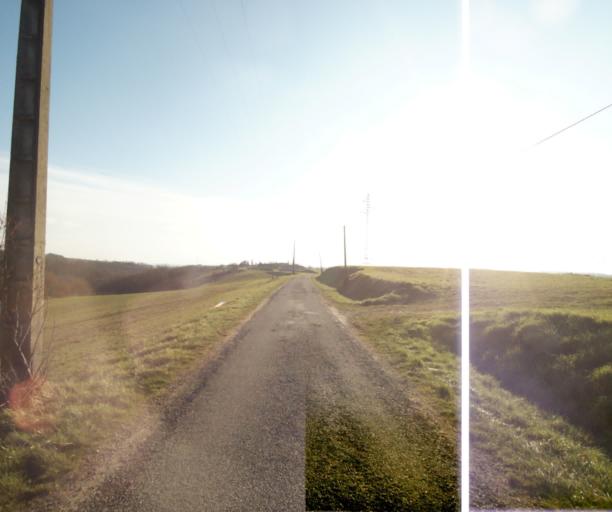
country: FR
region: Midi-Pyrenees
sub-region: Departement du Tarn-et-Garonne
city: Moissac
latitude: 44.1435
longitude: 1.1121
